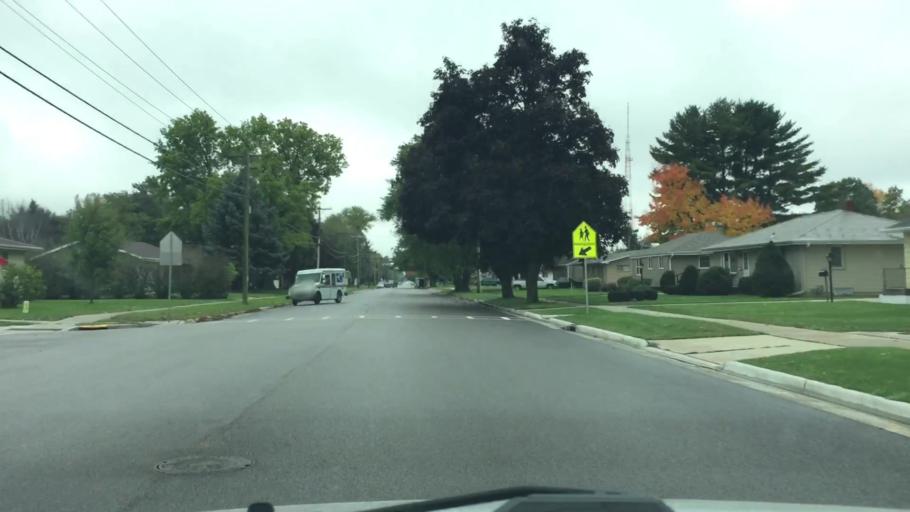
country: US
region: Wisconsin
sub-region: Rock County
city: Janesville
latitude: 42.6633
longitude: -89.0414
